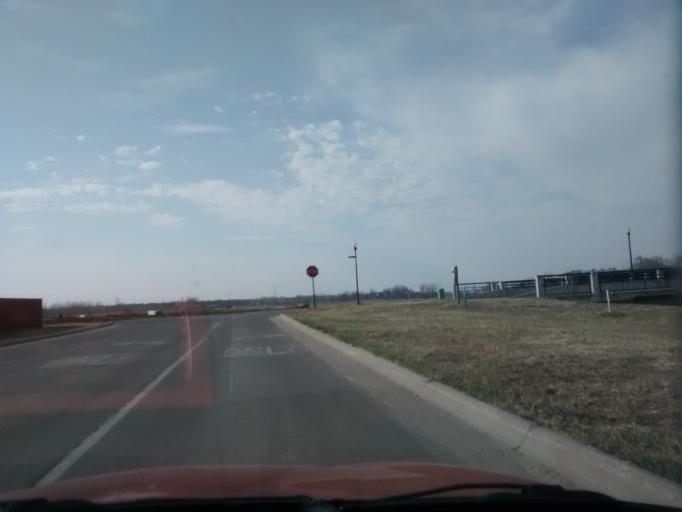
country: US
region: Nebraska
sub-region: Sarpy County
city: Offutt Air Force Base
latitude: 41.1454
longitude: -95.9786
